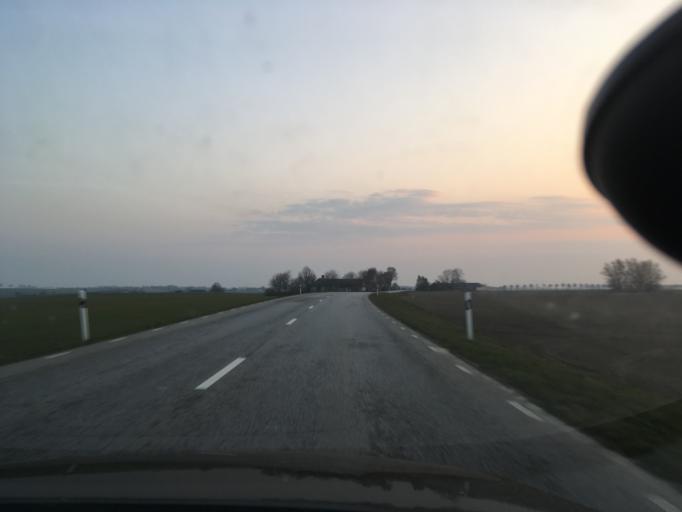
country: SE
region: Skane
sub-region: Ystads Kommun
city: Kopingebro
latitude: 55.4638
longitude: 14.0357
